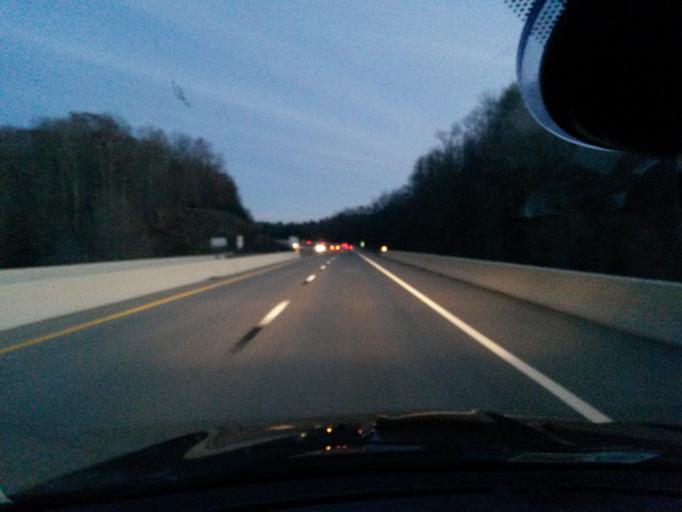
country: US
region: West Virginia
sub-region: Raleigh County
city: Shady Spring
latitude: 37.7671
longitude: -81.0378
